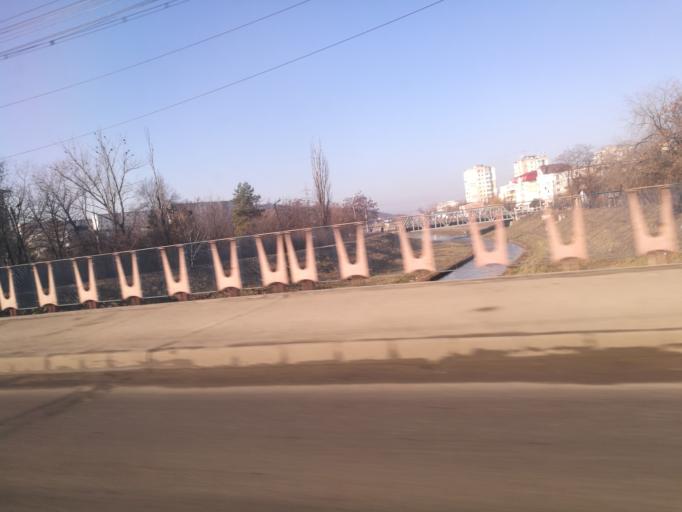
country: RO
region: Iasi
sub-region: Municipiul Iasi
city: Iasi
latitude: 47.1577
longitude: 27.5748
